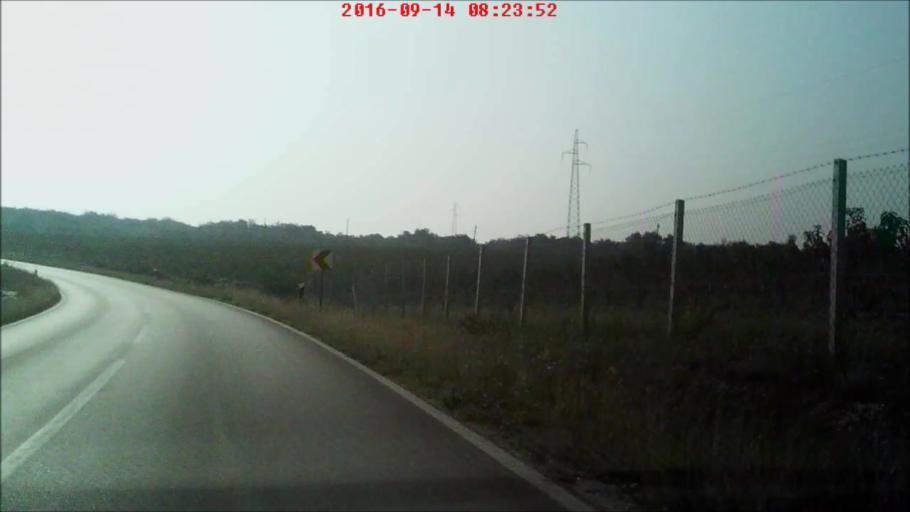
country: HR
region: Zadarska
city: Vrsi
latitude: 44.2094
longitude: 15.2363
